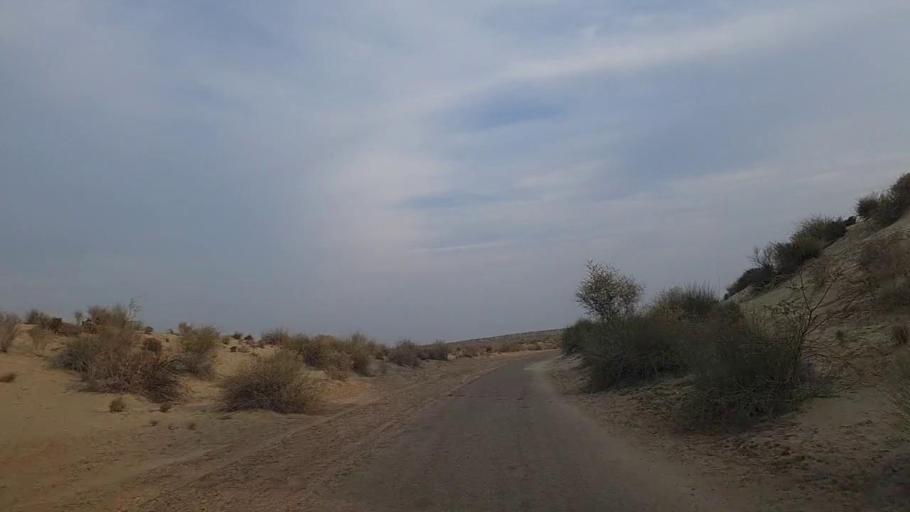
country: PK
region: Sindh
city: Jam Sahib
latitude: 26.4912
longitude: 68.5525
